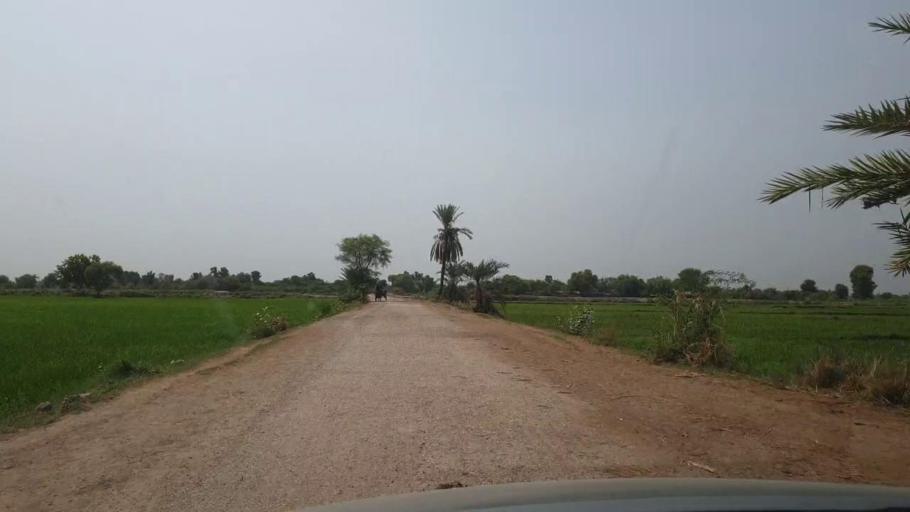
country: PK
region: Sindh
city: Madeji
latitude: 27.8000
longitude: 68.5396
